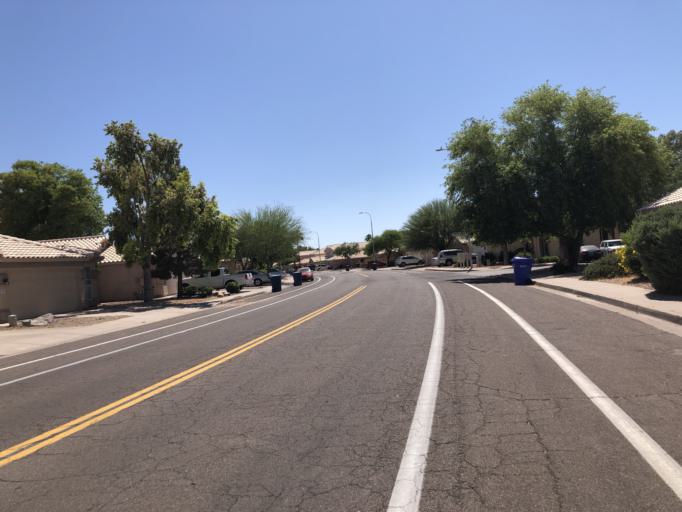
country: US
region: Arizona
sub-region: Maricopa County
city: Guadalupe
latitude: 33.3160
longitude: -111.9209
